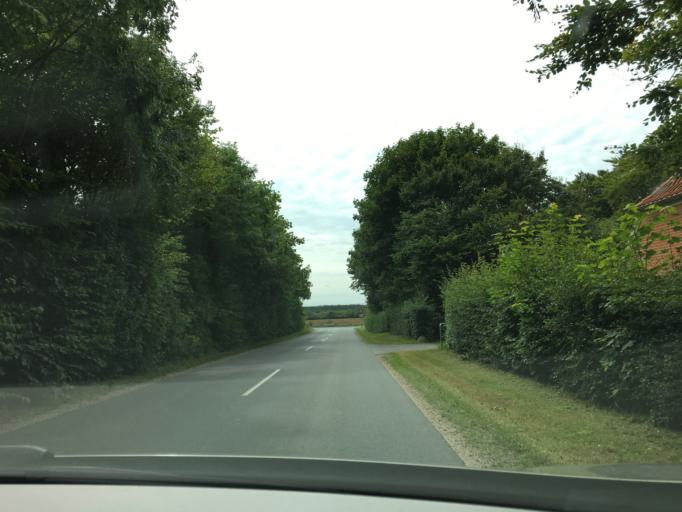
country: DK
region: South Denmark
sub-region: Varde Kommune
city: Oksbol
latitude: 55.7272
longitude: 8.2510
